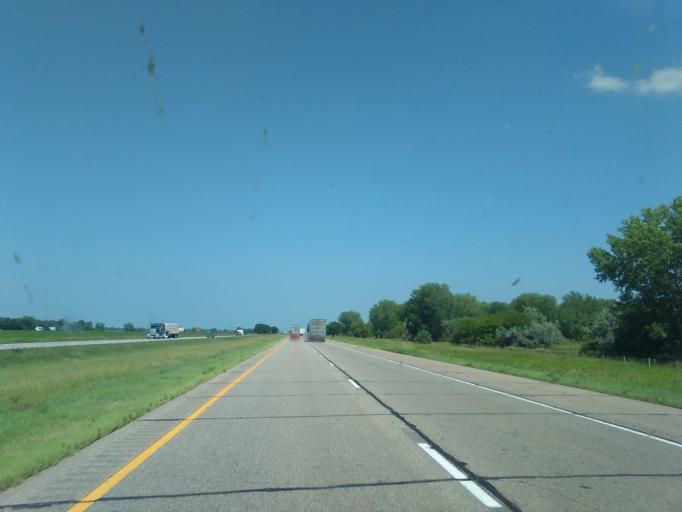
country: US
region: Nebraska
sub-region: Buffalo County
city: Kearney
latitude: 40.6726
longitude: -99.1898
